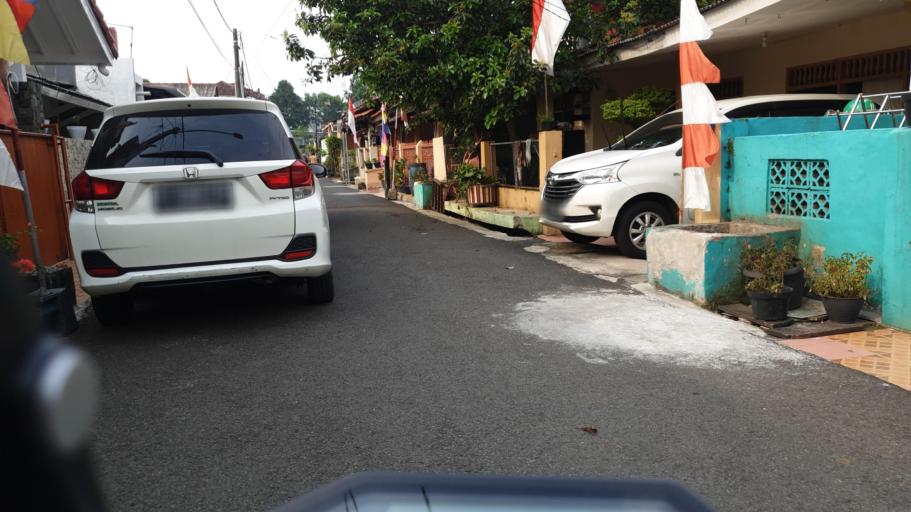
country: ID
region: West Java
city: Depok
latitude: -6.3396
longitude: 106.8307
